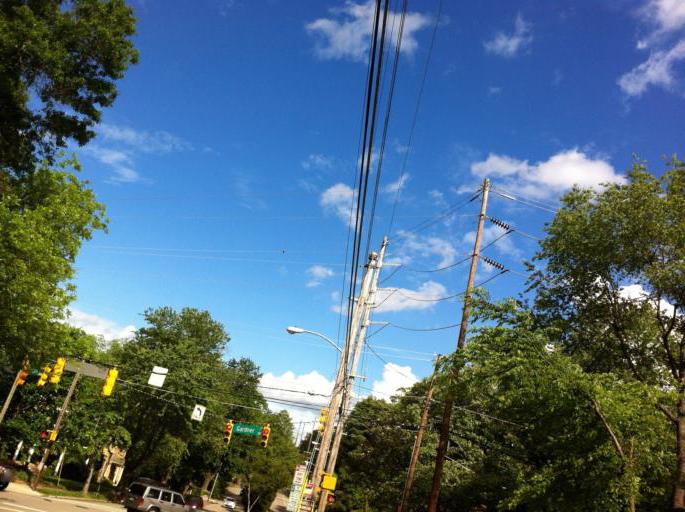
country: US
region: North Carolina
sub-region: Wake County
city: West Raleigh
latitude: 35.7904
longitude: -78.6708
